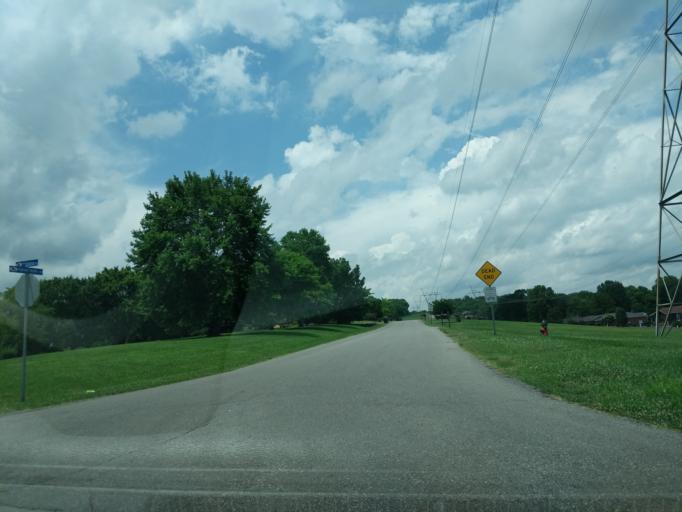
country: US
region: Tennessee
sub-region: Davidson County
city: Goodlettsville
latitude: 36.3037
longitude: -86.7260
